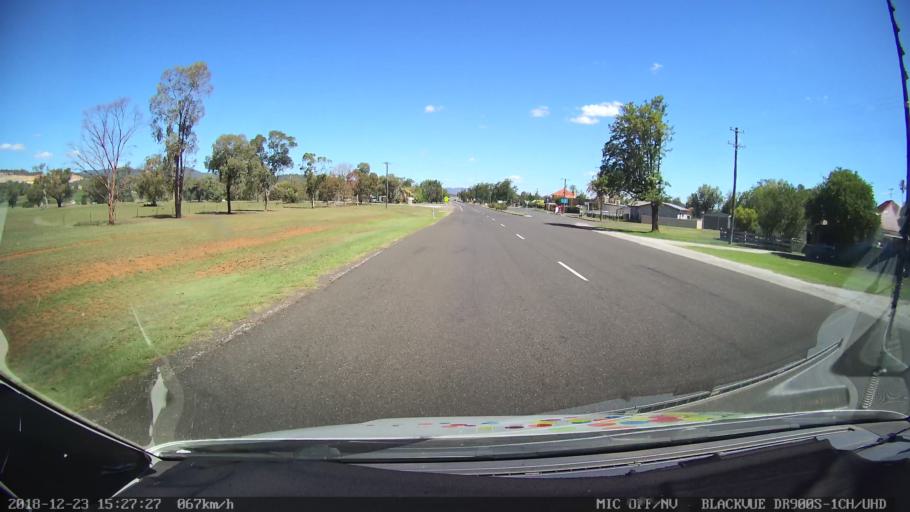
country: AU
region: New South Wales
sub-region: Tamworth Municipality
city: East Tamworth
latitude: -30.9277
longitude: 150.8454
